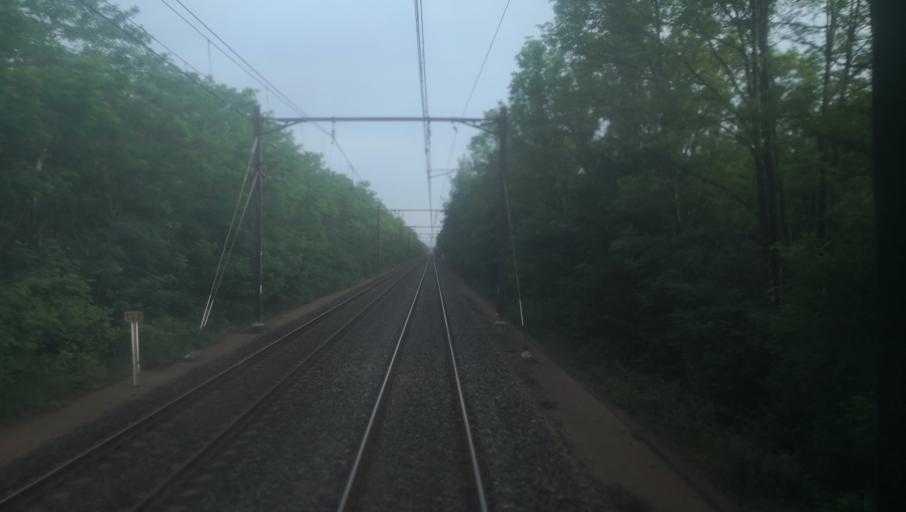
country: FR
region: Centre
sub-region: Departement du Loiret
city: Menestreau-en-Villette
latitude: 47.6571
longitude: 1.9762
